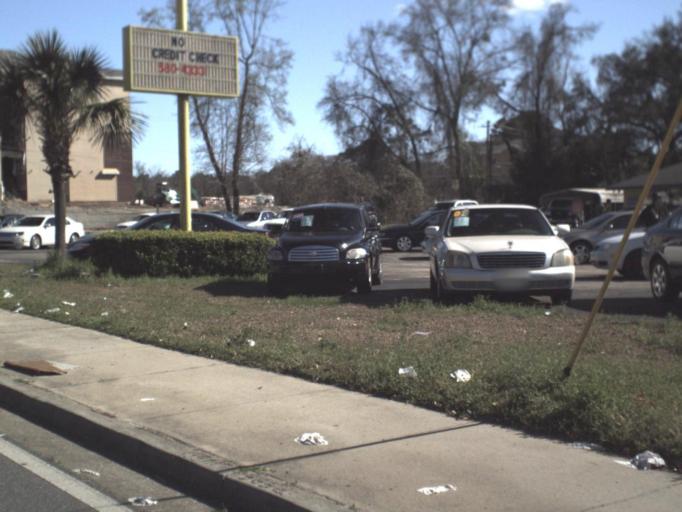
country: US
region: Florida
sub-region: Leon County
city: Tallahassee
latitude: 30.4509
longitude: -84.3340
